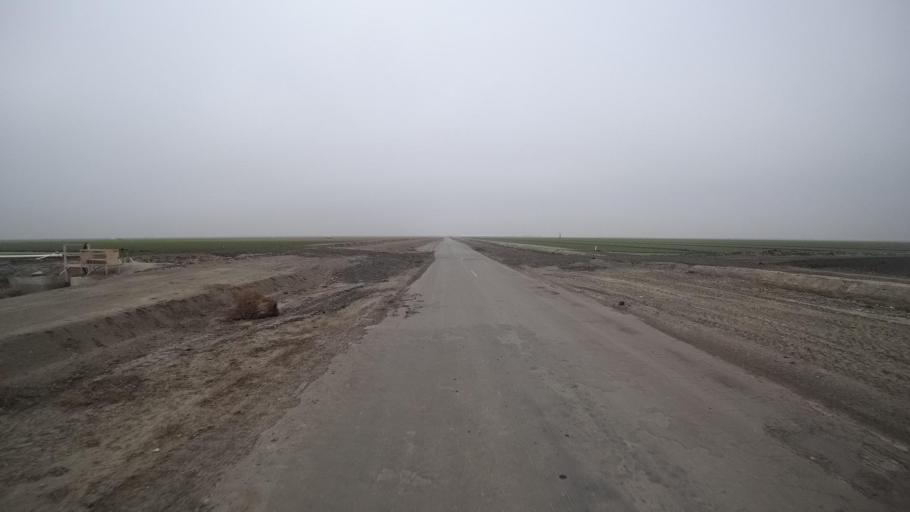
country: US
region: California
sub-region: Kern County
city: Rosedale
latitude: 35.1869
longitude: -119.1992
